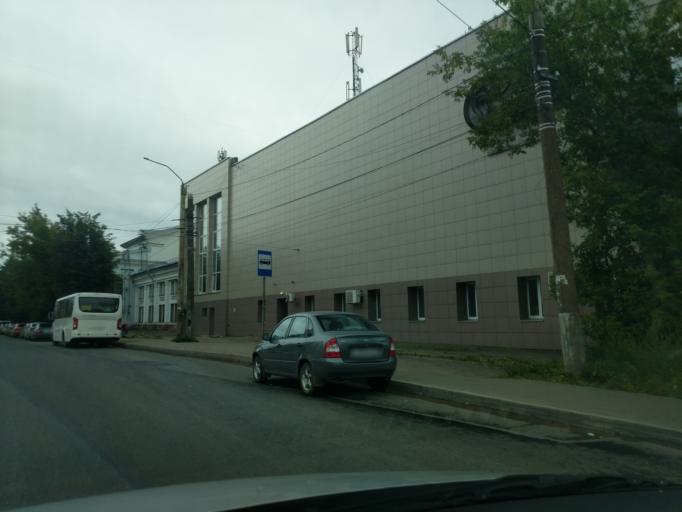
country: RU
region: Kirov
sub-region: Kirovo-Chepetskiy Rayon
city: Kirov
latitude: 58.6353
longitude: 49.6117
